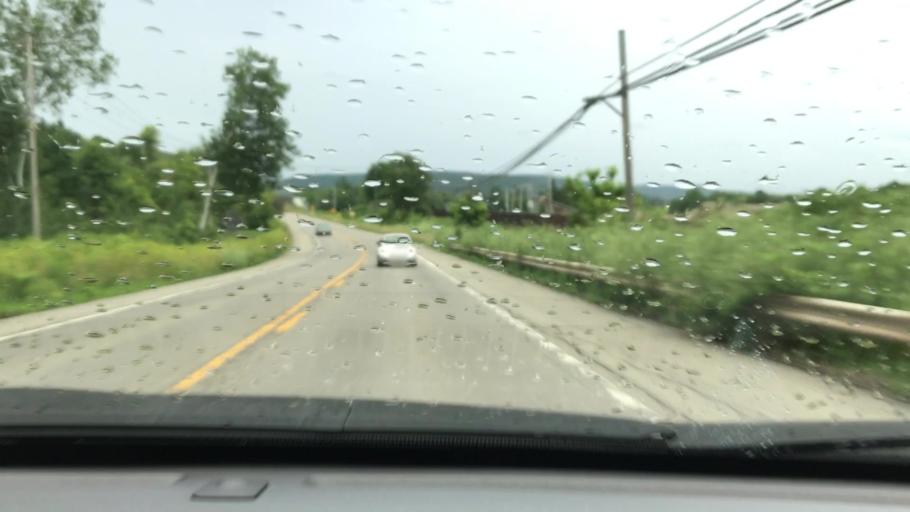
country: US
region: New York
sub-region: Cattaraugus County
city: Salamanca
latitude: 42.1901
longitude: -78.6734
